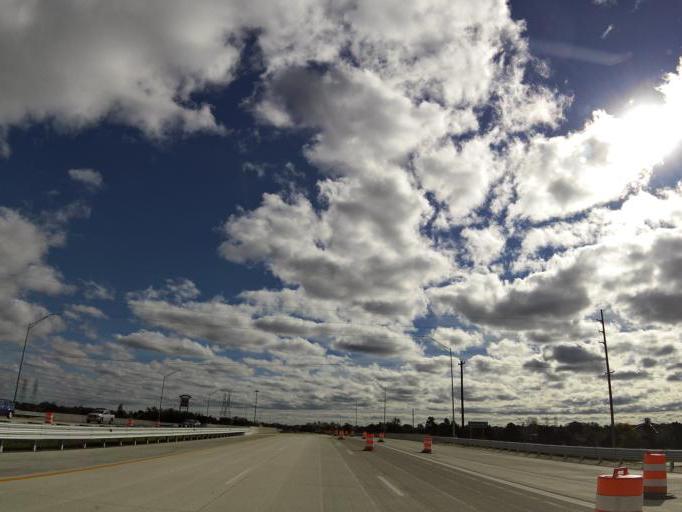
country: US
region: Michigan
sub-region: Genesee County
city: Burton
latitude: 43.0137
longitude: -83.6362
